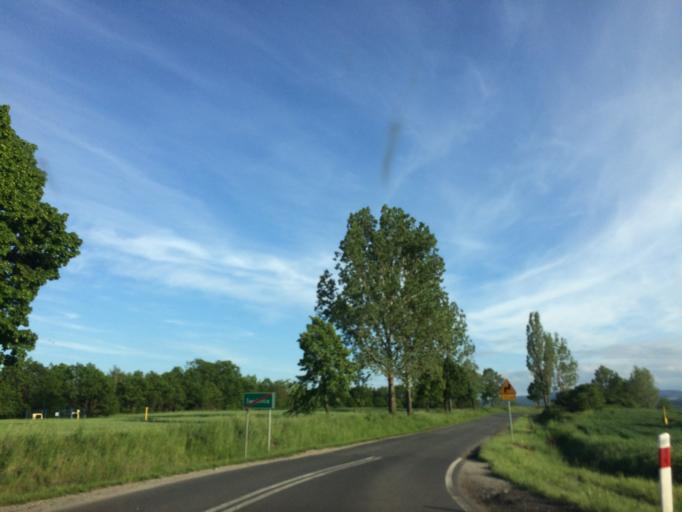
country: PL
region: Lower Silesian Voivodeship
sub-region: Powiat swidnicki
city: Swidnica
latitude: 50.8121
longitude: 16.4925
